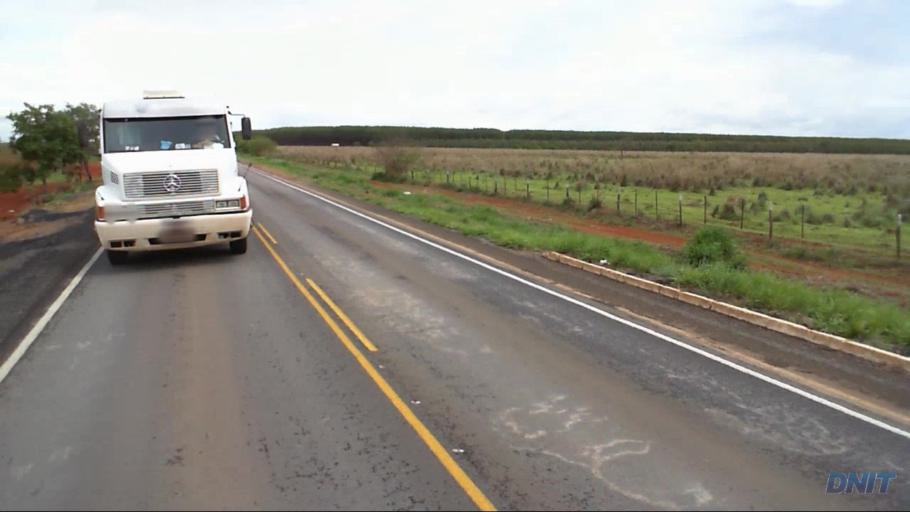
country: BR
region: Goias
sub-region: Padre Bernardo
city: Padre Bernardo
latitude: -15.2772
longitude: -48.2608
